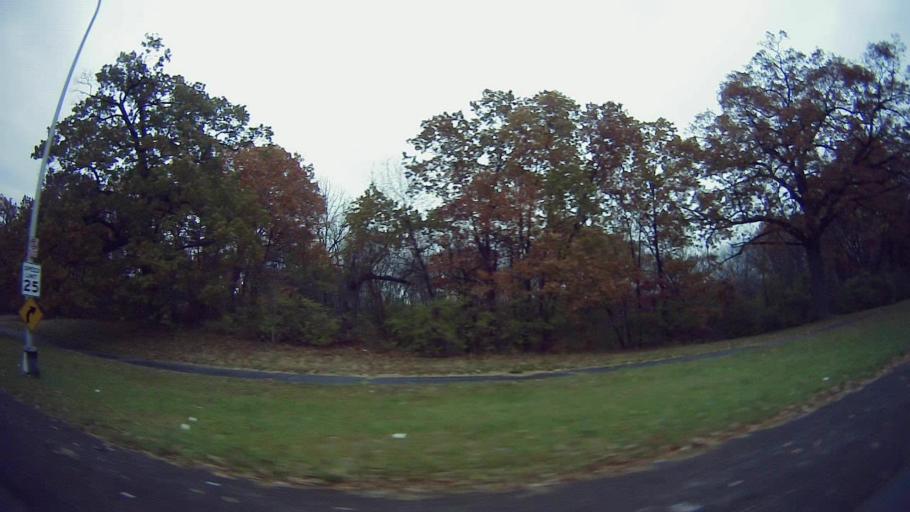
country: US
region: Michigan
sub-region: Wayne County
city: Dearborn Heights
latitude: 42.3560
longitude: -83.2611
